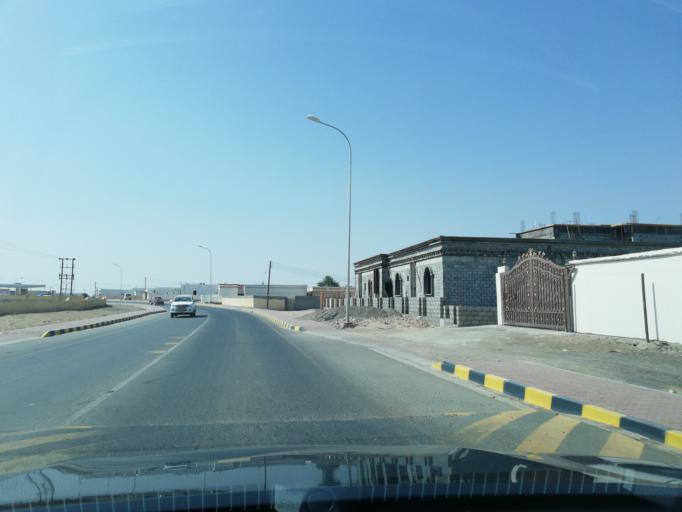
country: OM
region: Muhafazat ad Dakhiliyah
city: Adam
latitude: 22.3015
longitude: 58.0729
